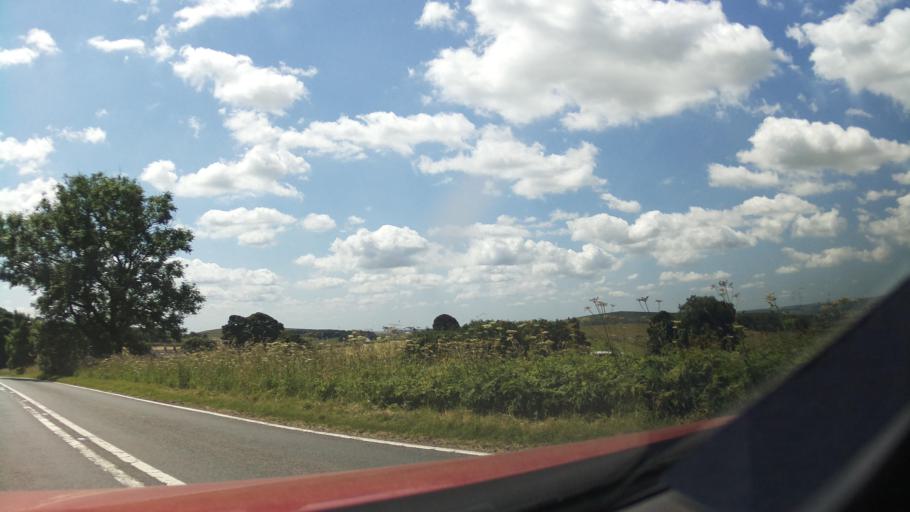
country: GB
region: England
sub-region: Derbyshire
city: Bakewell
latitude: 53.1343
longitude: -1.7540
